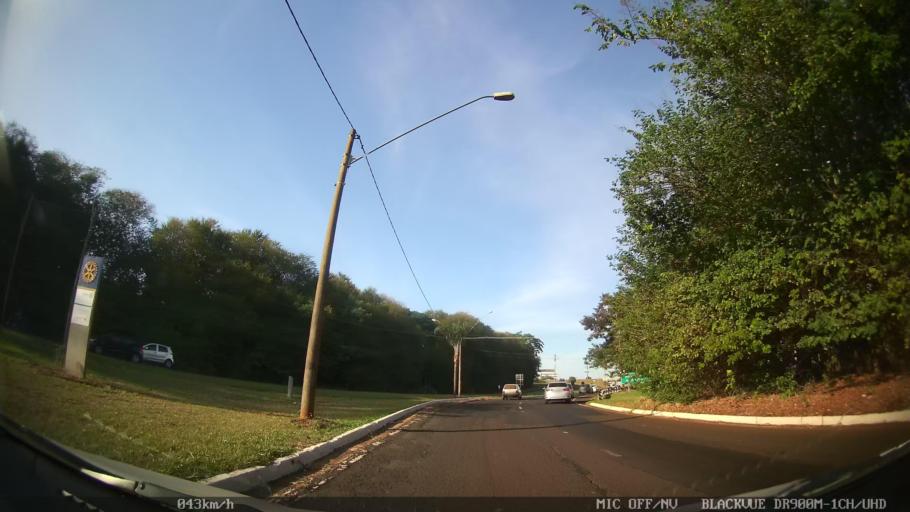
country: BR
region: Sao Paulo
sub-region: Ribeirao Preto
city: Ribeirao Preto
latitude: -21.2192
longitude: -47.8158
